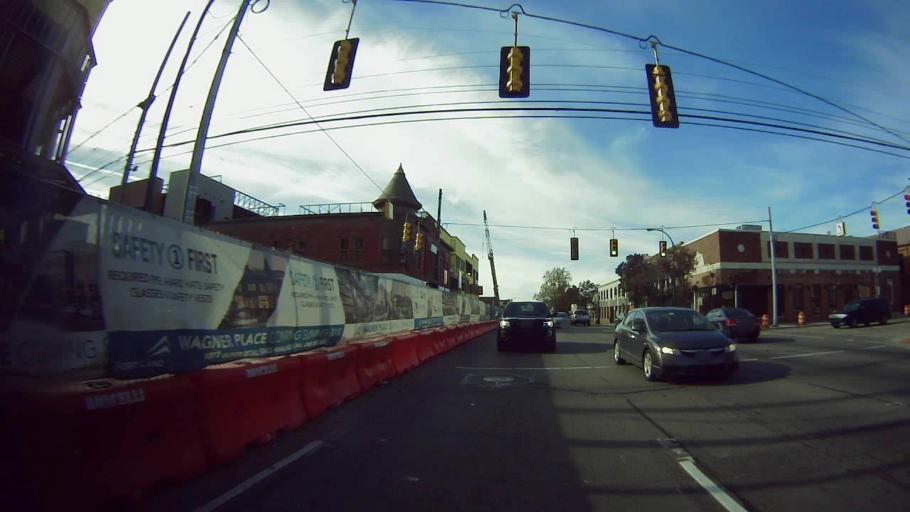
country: US
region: Michigan
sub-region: Wayne County
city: Dearborn Heights
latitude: 42.3062
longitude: -83.2438
